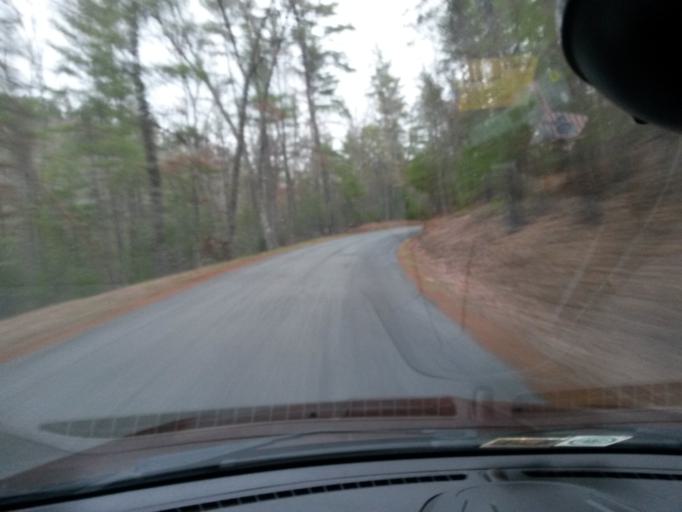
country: US
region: Virginia
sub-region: Bath County
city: Warm Springs
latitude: 37.9944
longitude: -79.7122
